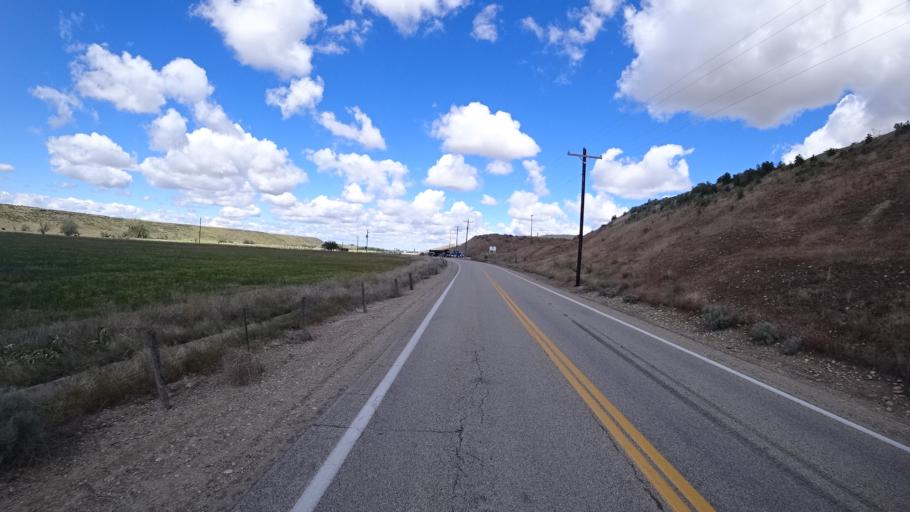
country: US
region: Idaho
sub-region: Ada County
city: Garden City
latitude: 43.4926
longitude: -116.2723
